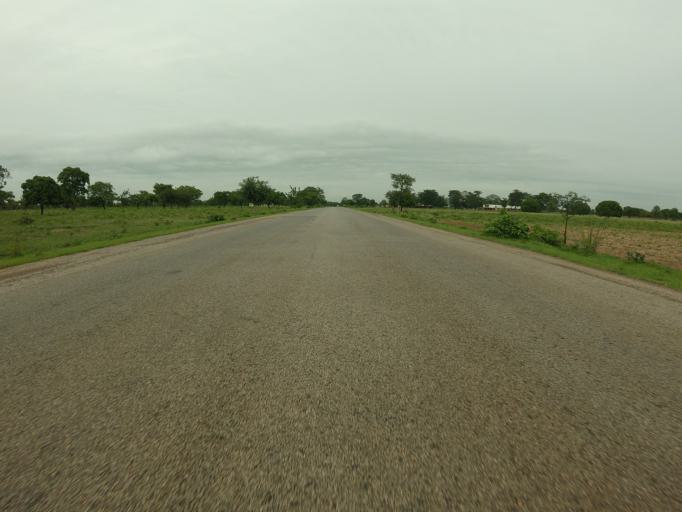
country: GH
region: Northern
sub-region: Yendi
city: Yendi
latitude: 9.5103
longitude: -0.0280
